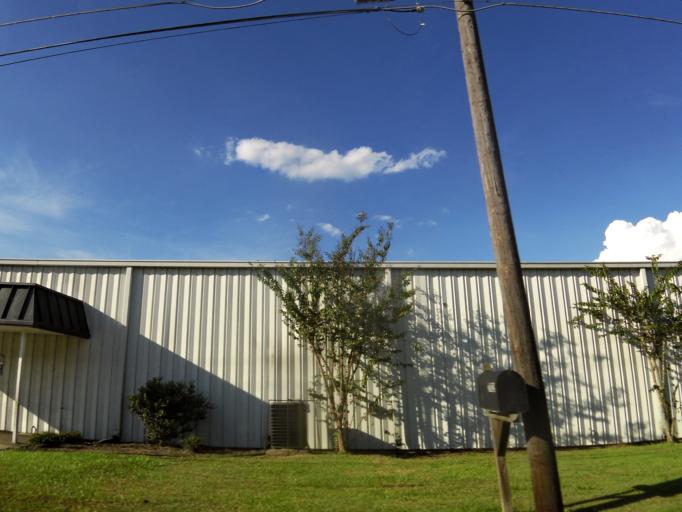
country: US
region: Georgia
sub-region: Brooks County
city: Quitman
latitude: 30.7795
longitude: -83.5541
